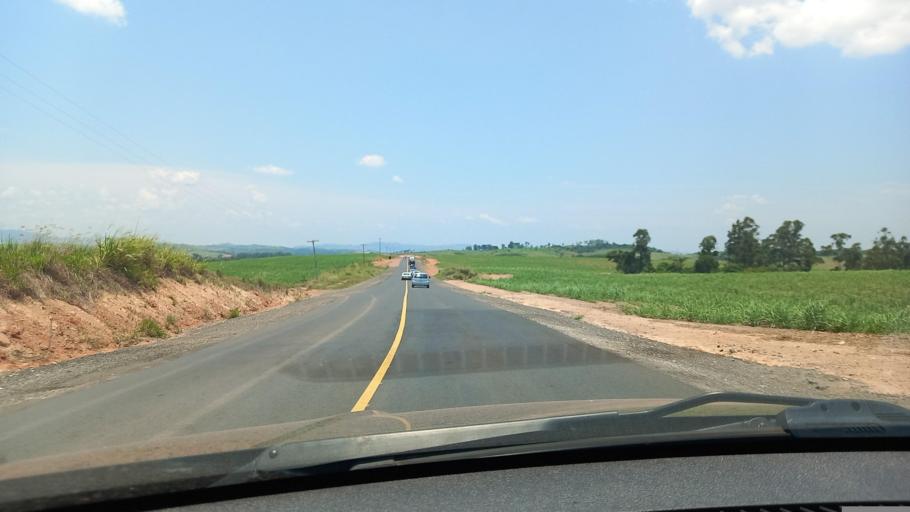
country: BR
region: Sao Paulo
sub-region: Itapira
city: Itapira
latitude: -22.3879
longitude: -46.8657
